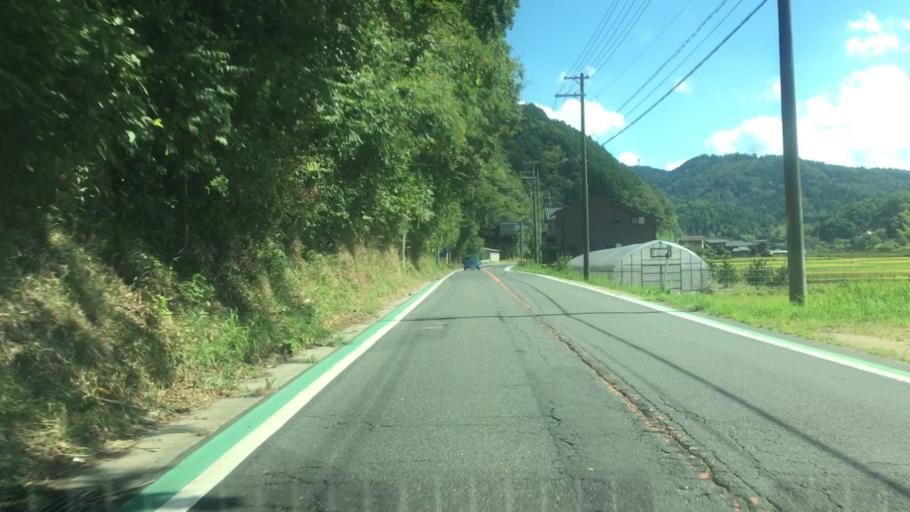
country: JP
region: Hyogo
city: Toyooka
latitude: 35.5989
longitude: 134.9040
